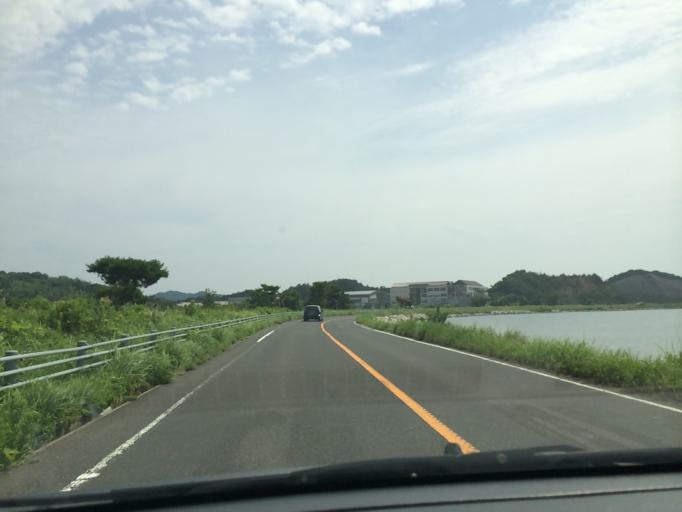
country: JP
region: Shimane
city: Sakaiminato
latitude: 35.5369
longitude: 133.1591
